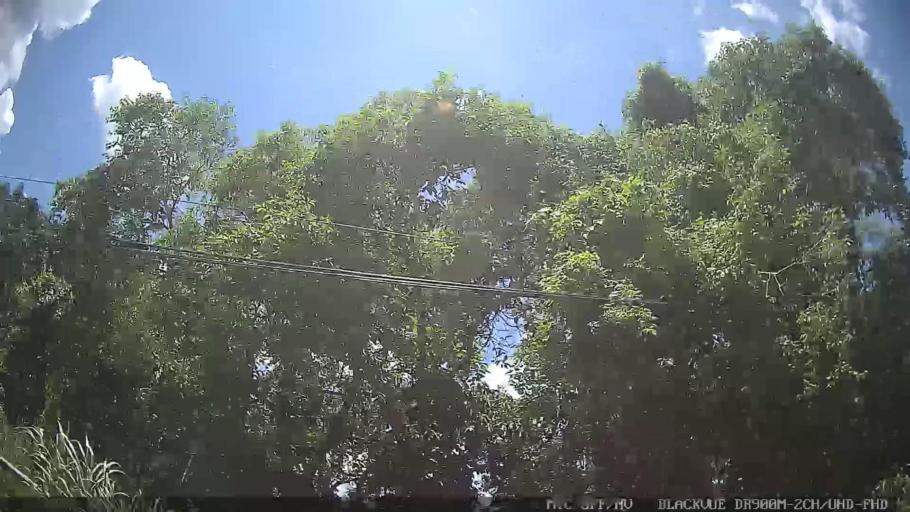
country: BR
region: Sao Paulo
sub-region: Amparo
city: Amparo
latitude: -22.6878
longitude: -46.7454
